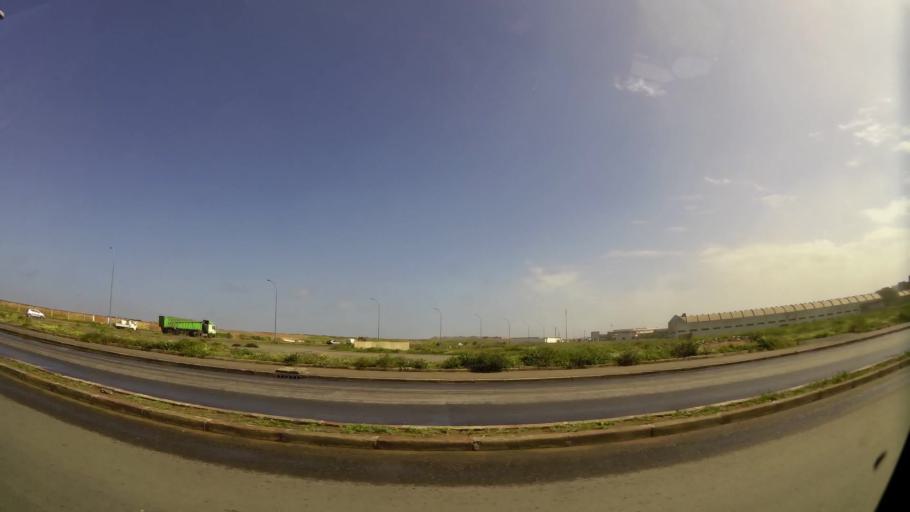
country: MA
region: Grand Casablanca
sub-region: Mediouna
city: Tit Mellil
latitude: 33.6277
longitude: -7.5159
